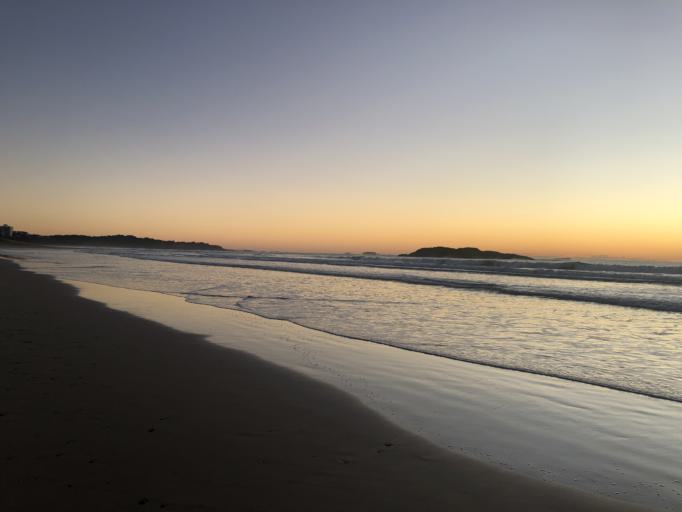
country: AU
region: New South Wales
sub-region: Coffs Harbour
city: Coffs Harbour
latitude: -30.2995
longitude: 153.1401
